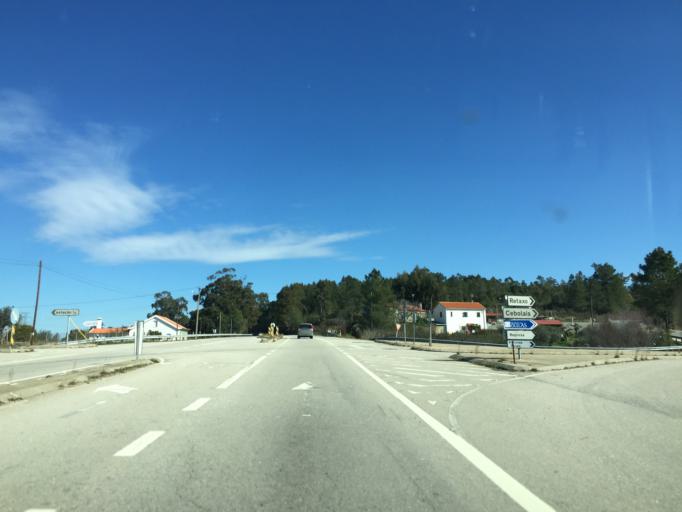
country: PT
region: Castelo Branco
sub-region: Castelo Branco
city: Castelo Branco
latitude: 39.7682
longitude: -7.5914
